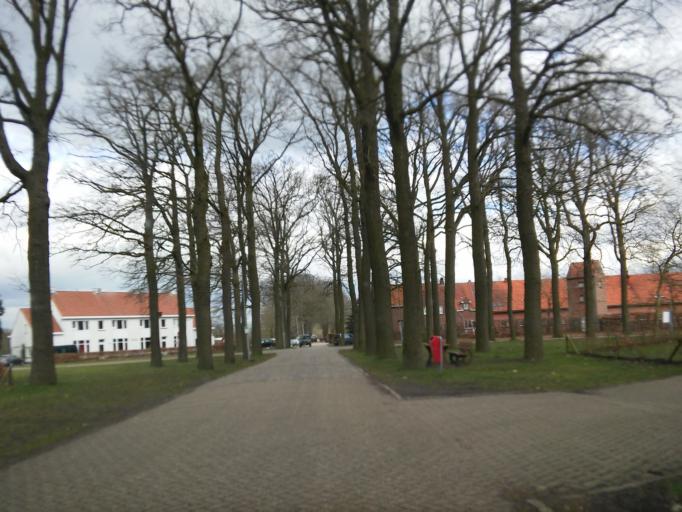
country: BE
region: Flanders
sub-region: Provincie Antwerpen
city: Merksplas
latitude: 51.4023
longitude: 4.8245
